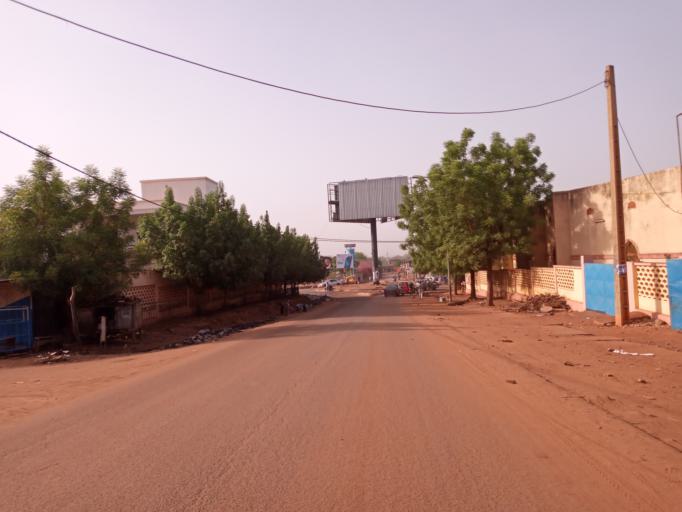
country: ML
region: Bamako
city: Bamako
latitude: 12.6622
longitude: -7.9786
